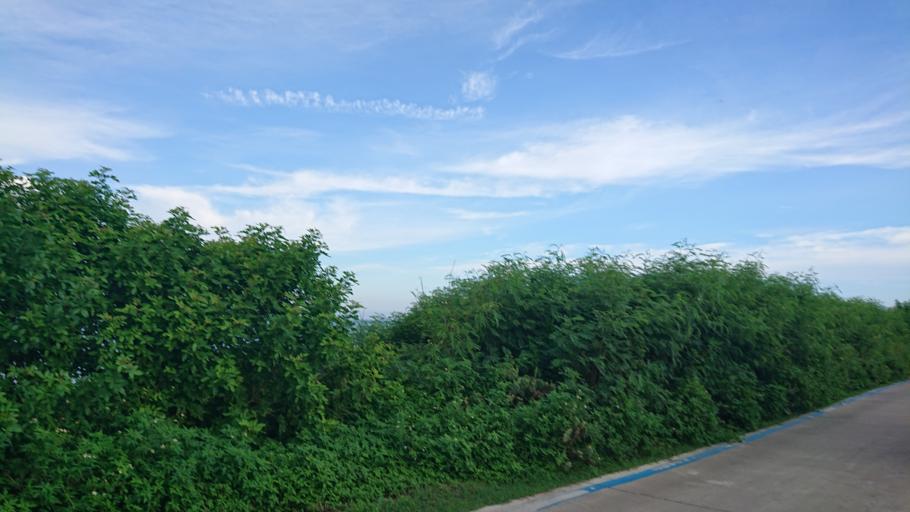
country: TW
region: Taiwan
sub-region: Penghu
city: Ma-kung
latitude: 23.5206
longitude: 119.6107
